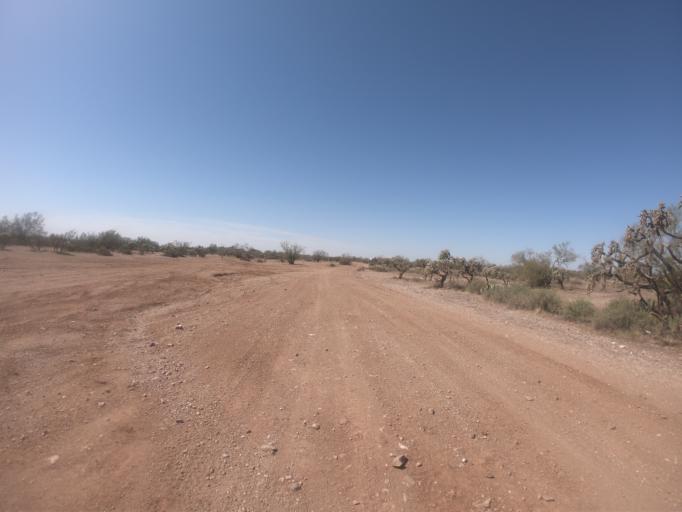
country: US
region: Arizona
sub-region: Pinal County
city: Gold Camp
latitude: 33.2482
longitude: -111.3071
